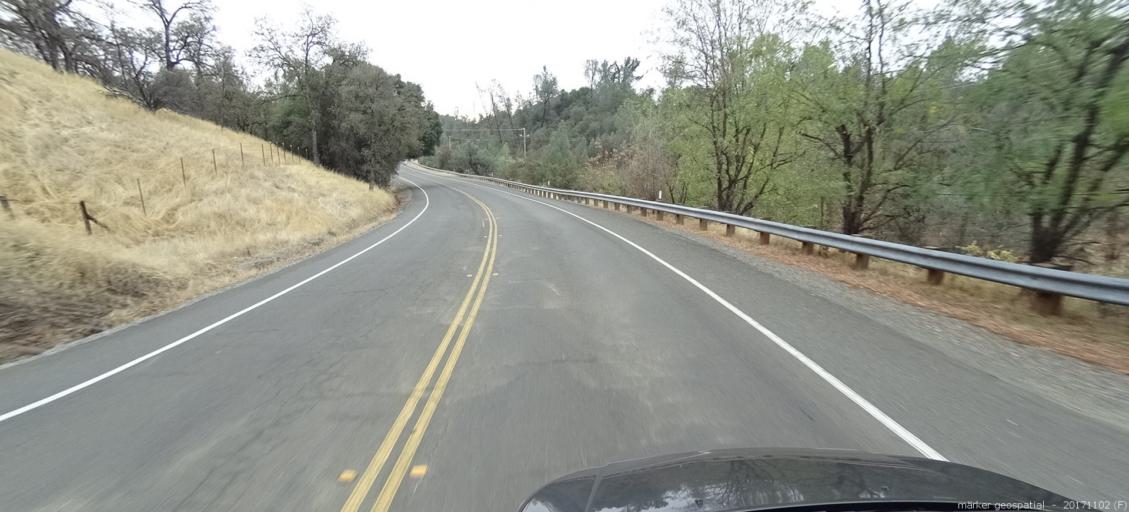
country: US
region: California
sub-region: Shasta County
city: Bella Vista
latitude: 40.6842
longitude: -122.2461
